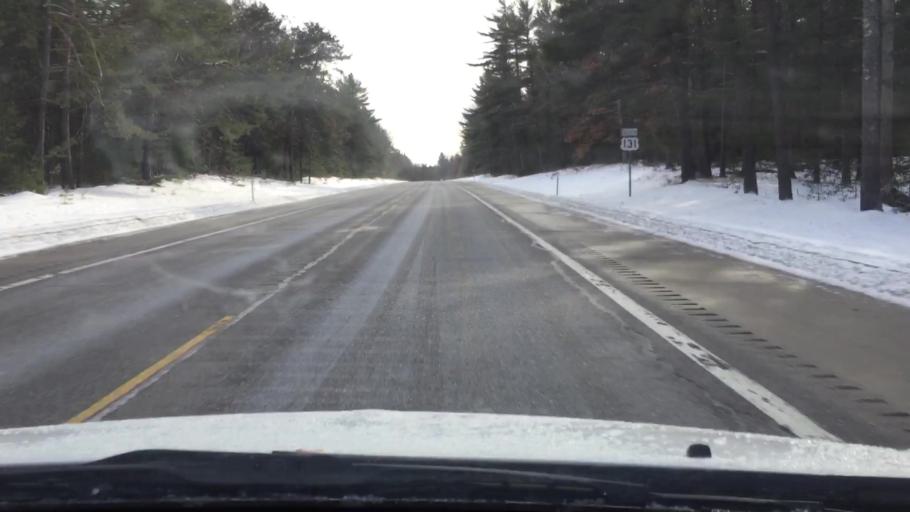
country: US
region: Michigan
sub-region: Wexford County
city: Manton
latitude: 44.5554
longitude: -85.3687
